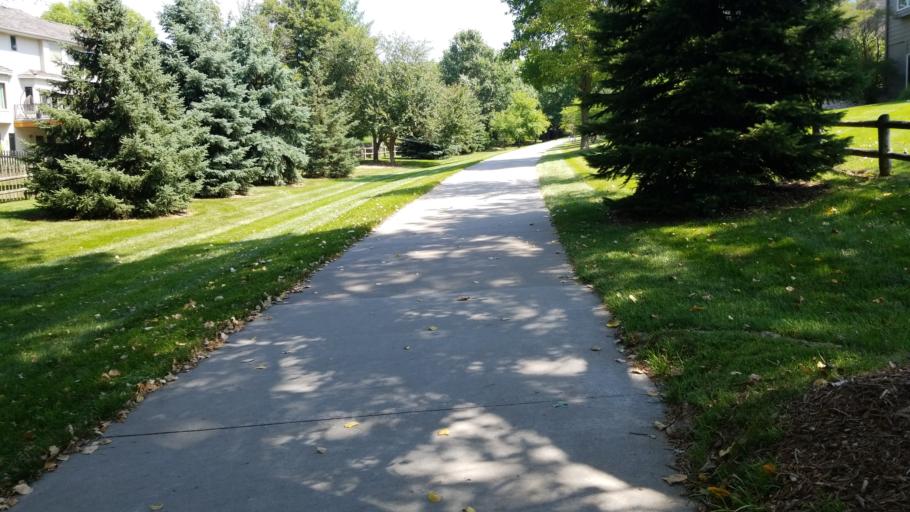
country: US
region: Nebraska
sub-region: Douglas County
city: Elkhorn
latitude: 41.2828
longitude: -96.1634
